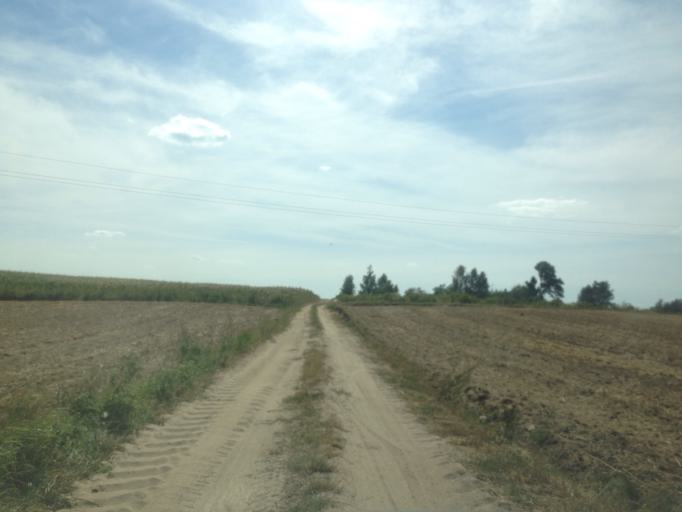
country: PL
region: Kujawsko-Pomorskie
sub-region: Powiat brodnicki
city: Gorzno
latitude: 53.2163
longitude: 19.6287
